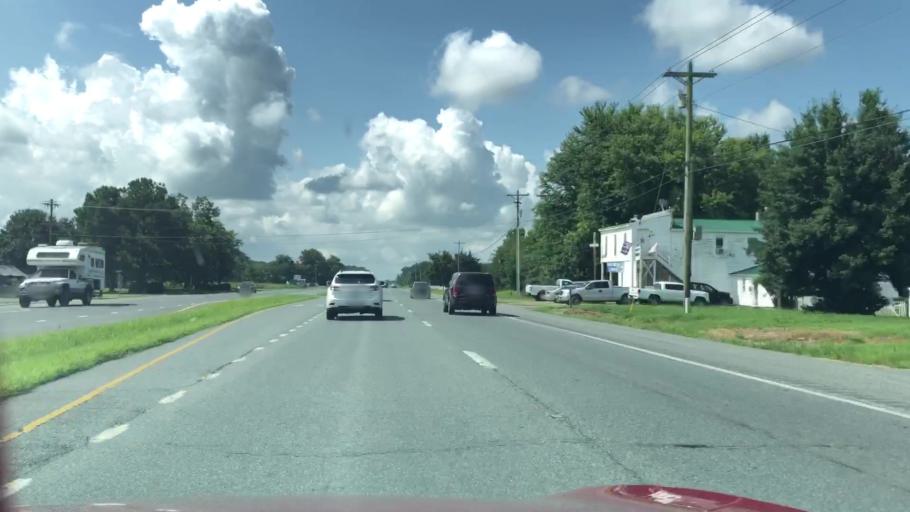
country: US
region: Virginia
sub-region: Accomack County
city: Accomac
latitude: 37.8006
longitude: -75.5964
